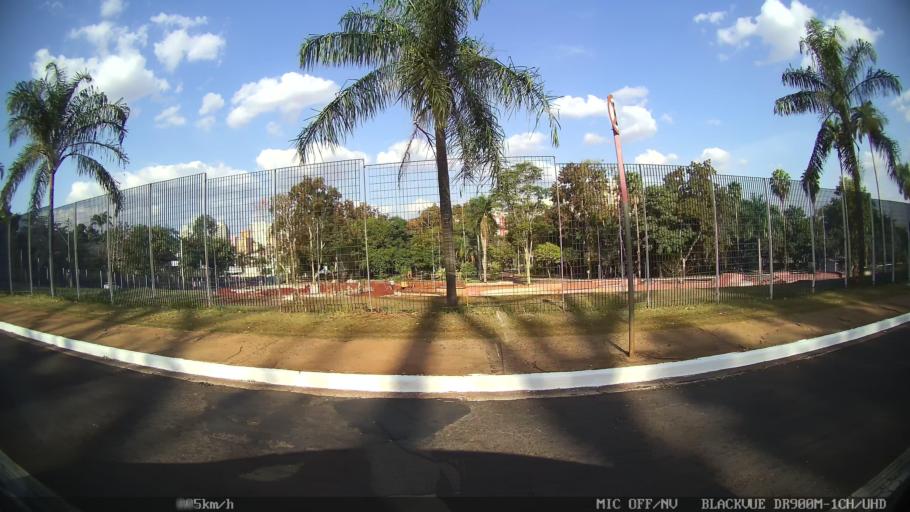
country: BR
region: Sao Paulo
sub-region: Ribeirao Preto
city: Ribeirao Preto
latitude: -21.1748
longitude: -47.8181
